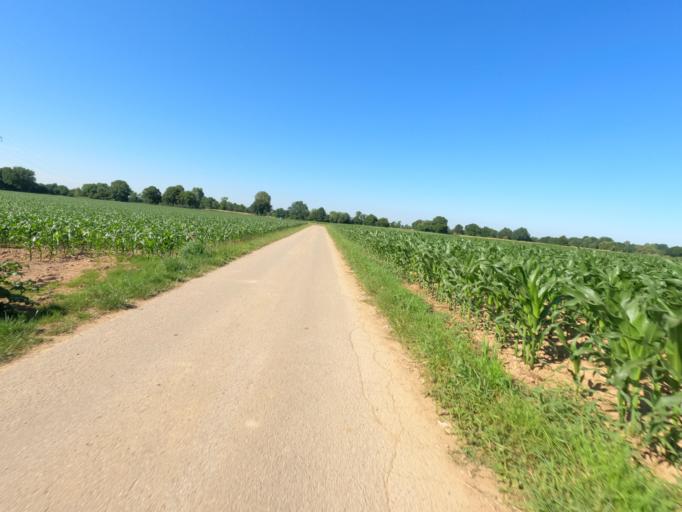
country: DE
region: North Rhine-Westphalia
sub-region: Regierungsbezirk Koln
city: Wassenberg
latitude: 51.0911
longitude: 6.1357
